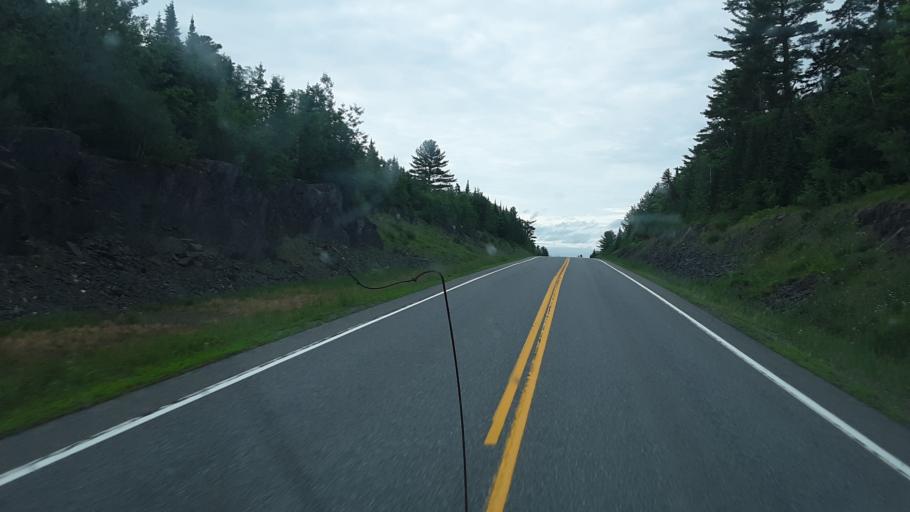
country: US
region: Maine
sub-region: Penobscot County
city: Patten
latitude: 46.4195
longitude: -68.3742
